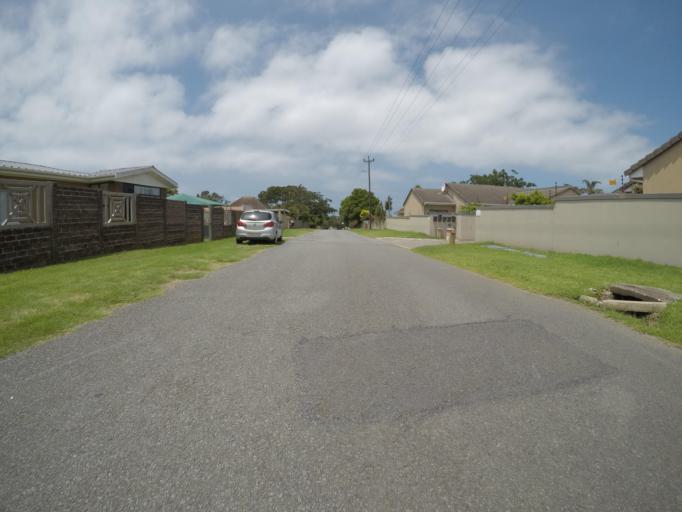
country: ZA
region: Eastern Cape
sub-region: Buffalo City Metropolitan Municipality
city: East London
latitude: -32.9397
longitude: 28.0134
